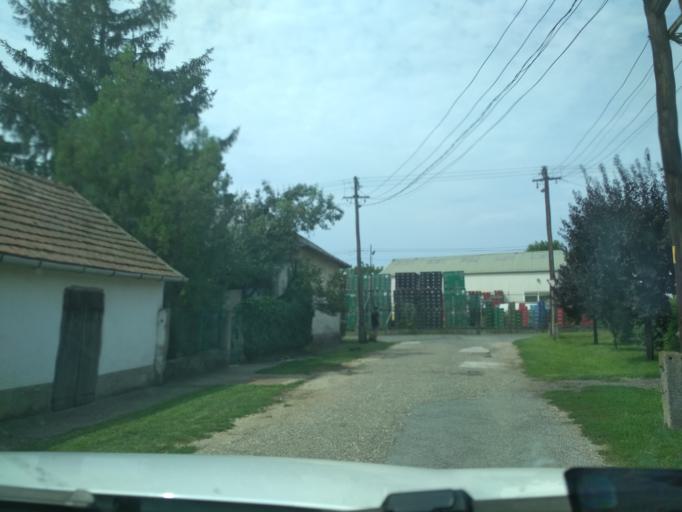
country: HU
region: Jasz-Nagykun-Szolnok
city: Tiszafured
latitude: 47.6101
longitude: 20.7626
